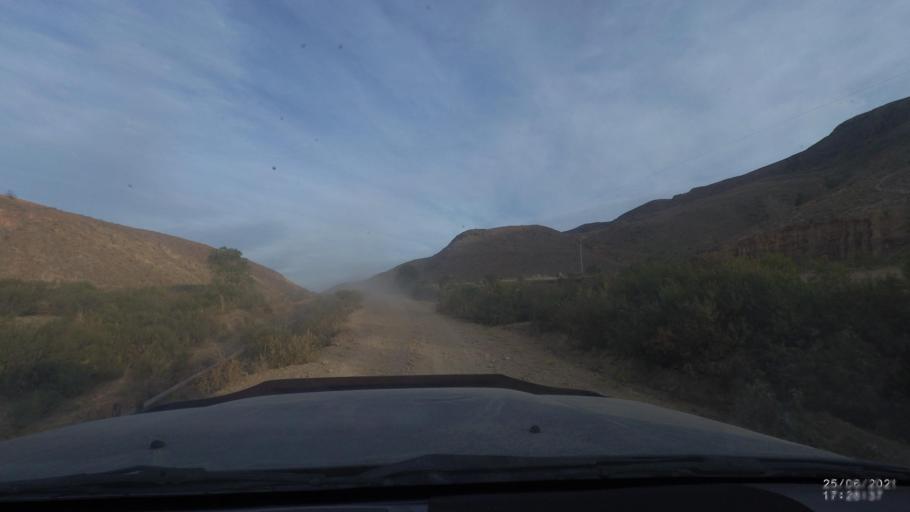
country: BO
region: Cochabamba
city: Mizque
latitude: -17.9273
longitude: -65.6693
